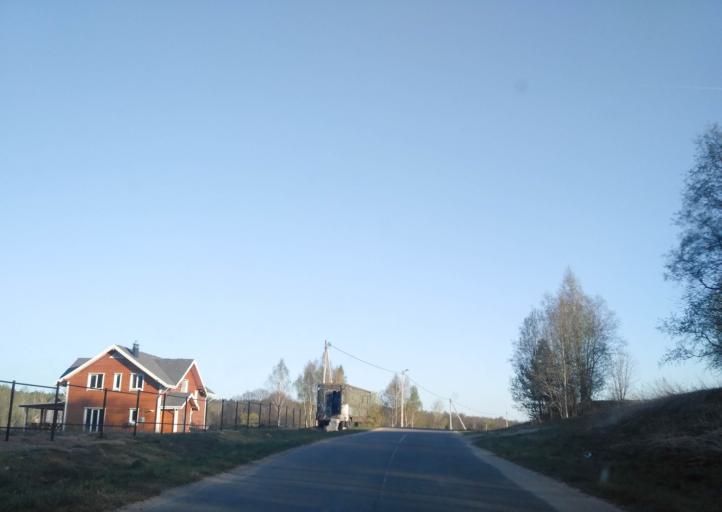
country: BY
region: Minsk
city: Pyatryshki
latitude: 54.1094
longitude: 27.1911
